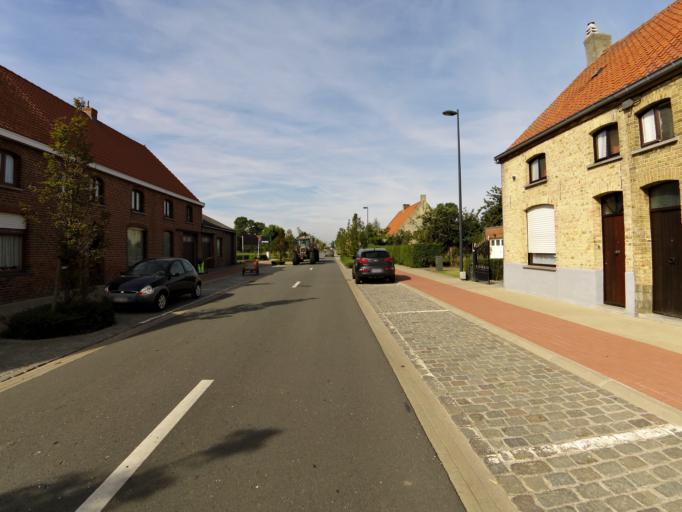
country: BE
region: Flanders
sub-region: Provincie West-Vlaanderen
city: Gistel
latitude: 51.1217
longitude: 2.9531
